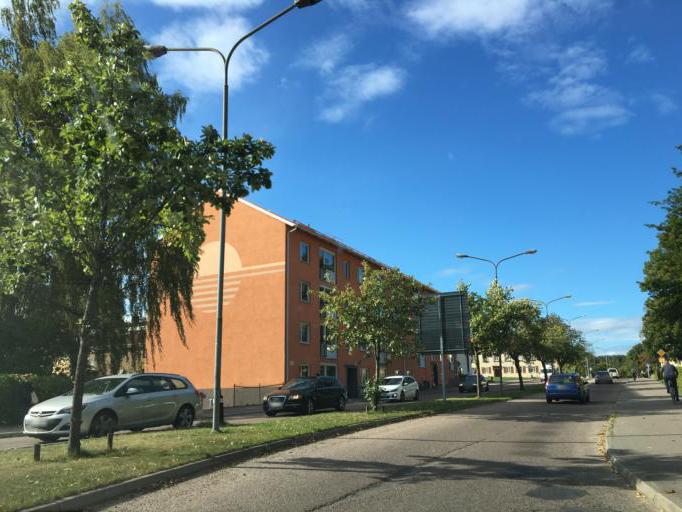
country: SE
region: Soedermanland
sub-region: Nykopings Kommun
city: Nykoping
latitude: 58.7545
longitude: 17.0032
